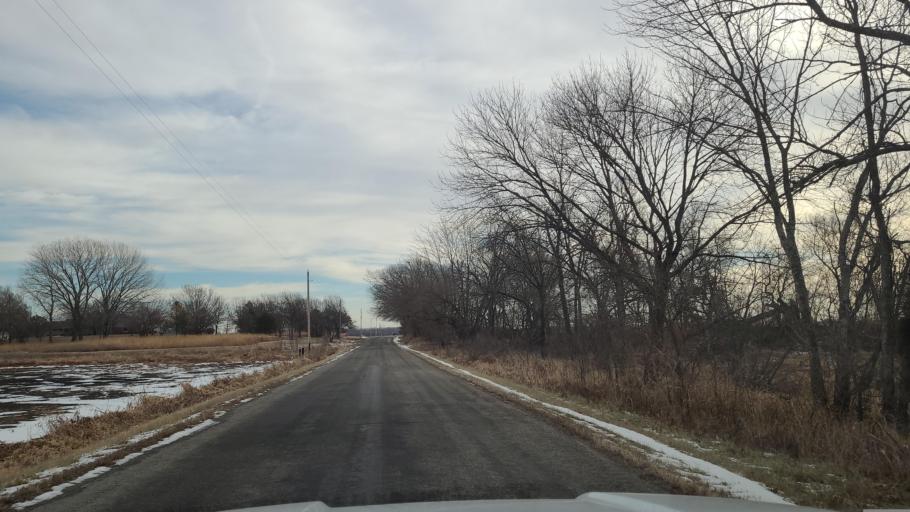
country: US
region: Kansas
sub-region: Douglas County
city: Lawrence
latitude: 39.0224
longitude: -95.3075
